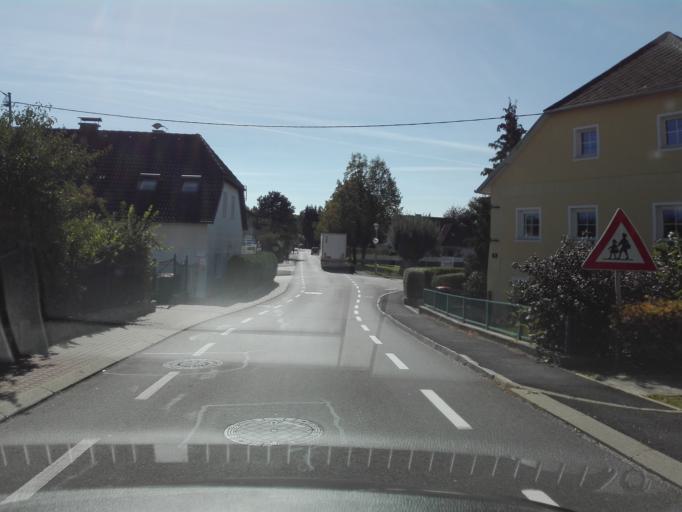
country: AT
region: Upper Austria
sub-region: Politischer Bezirk Linz-Land
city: Sankt Florian
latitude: 48.2047
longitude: 14.3796
